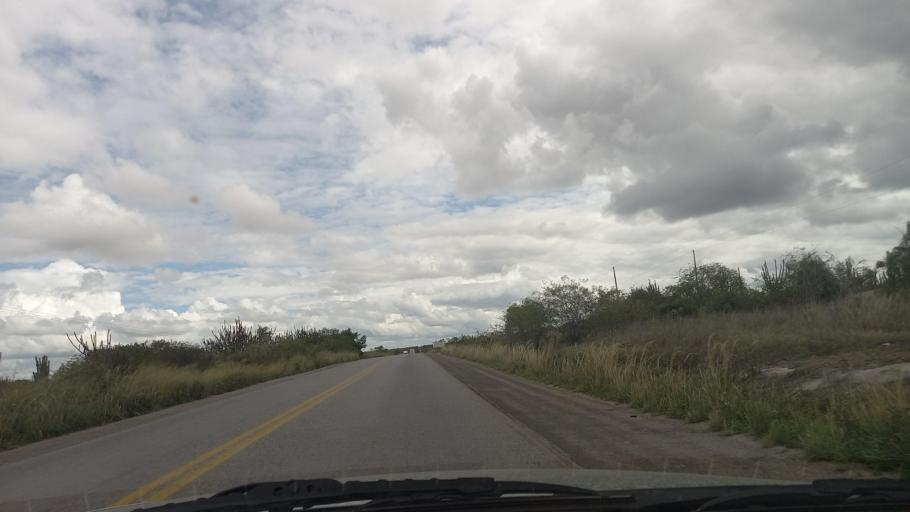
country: BR
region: Pernambuco
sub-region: Cachoeirinha
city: Cachoeirinha
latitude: -8.3457
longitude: -36.1652
